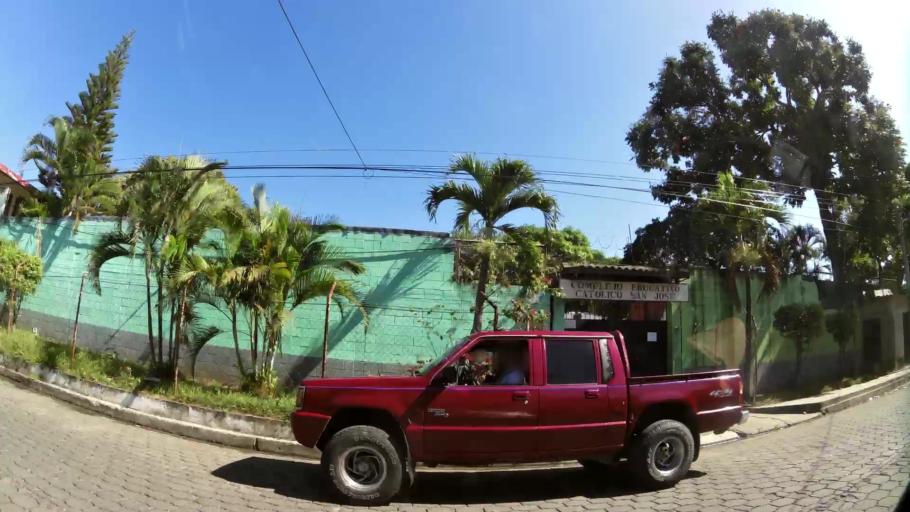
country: SV
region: La Libertad
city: Santa Tecla
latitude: 13.7291
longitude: -89.3699
